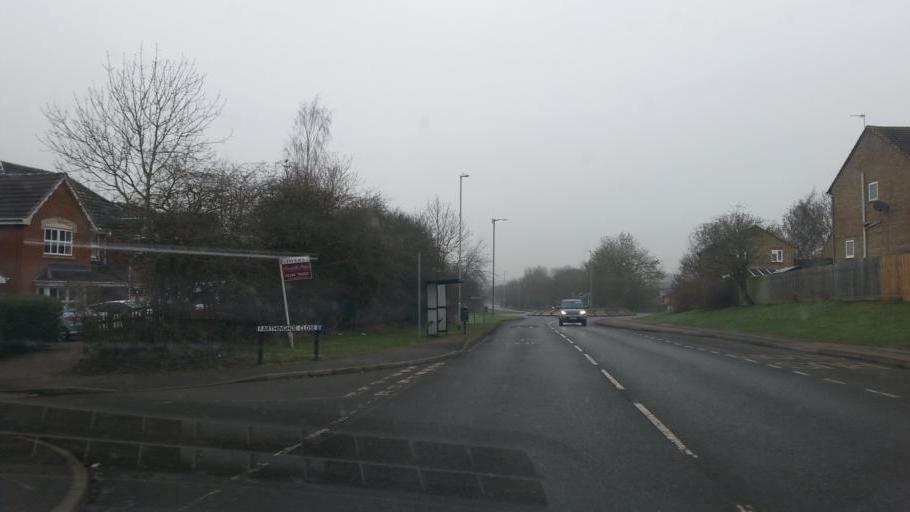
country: GB
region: England
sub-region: Northamptonshire
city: Brackley
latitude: 52.0304
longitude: -1.1597
